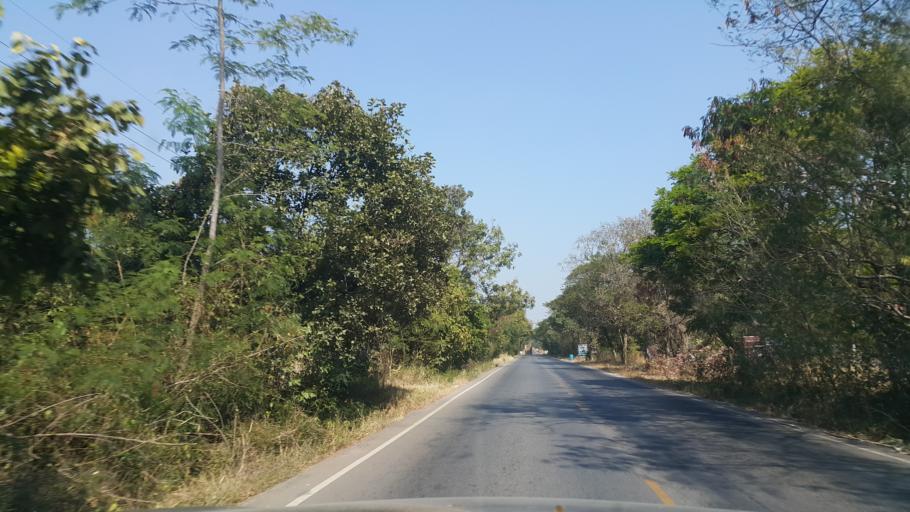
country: TH
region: Chaiyaphum
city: Khon Sawan
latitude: 15.8876
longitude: 102.2464
